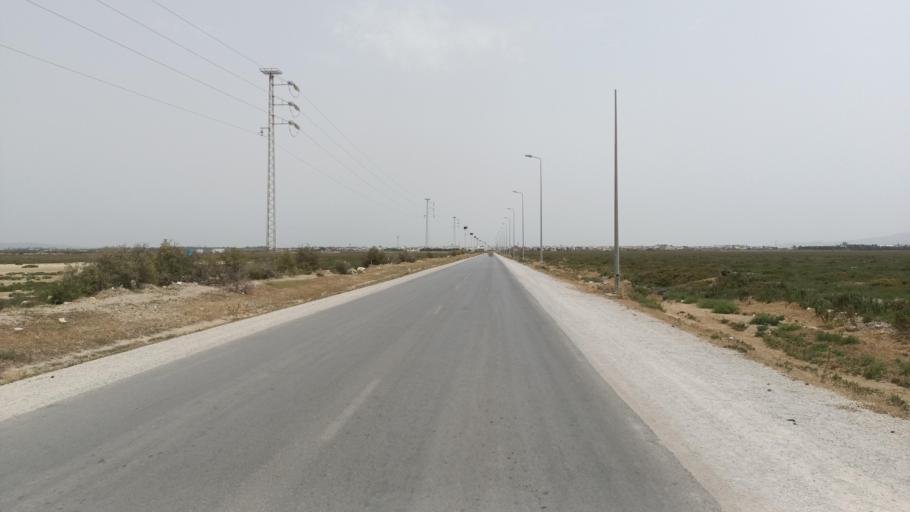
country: TN
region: Nabul
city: Manzil Bu Zalafah
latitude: 36.7218
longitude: 10.4735
